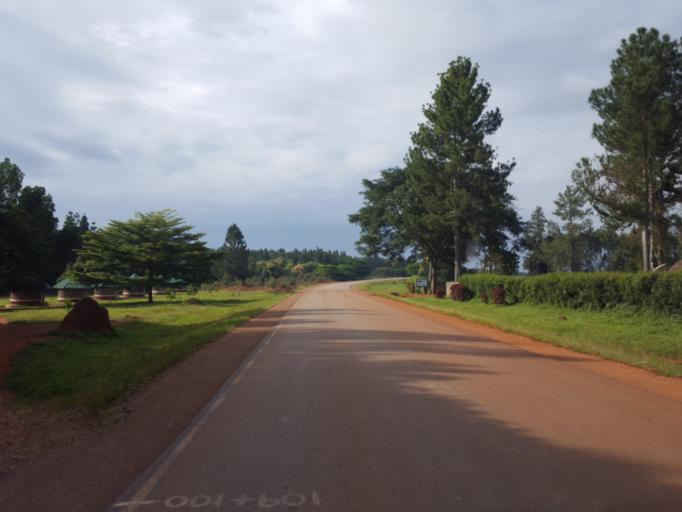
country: UG
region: Central Region
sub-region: Kyankwanzi District
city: Kyankwanzi
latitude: 1.2097
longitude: 31.5594
